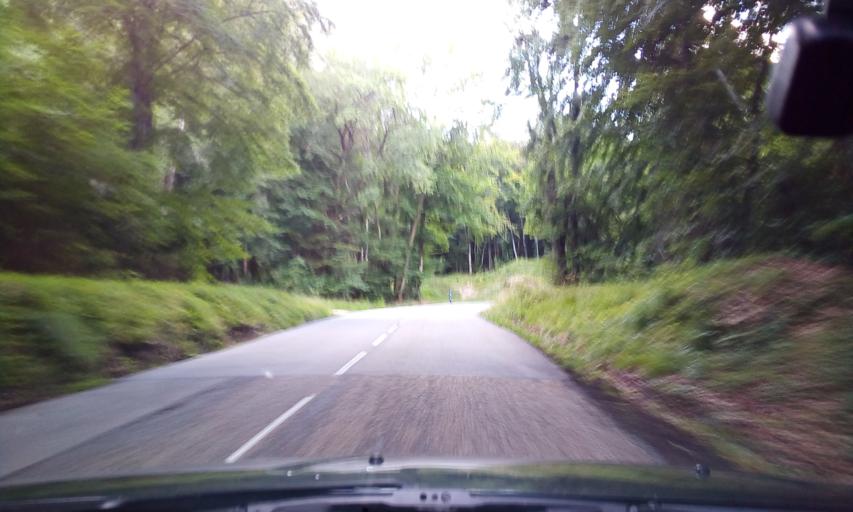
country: FR
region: Rhone-Alpes
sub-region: Departement de l'Isere
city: Chapareillan
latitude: 45.4777
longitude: 5.9459
